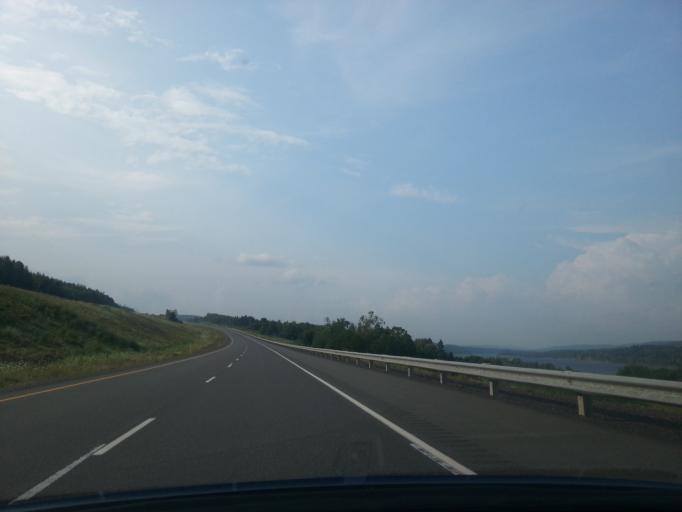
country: US
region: Maine
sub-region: Aroostook County
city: Fort Fairfield
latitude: 46.6776
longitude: -67.7297
